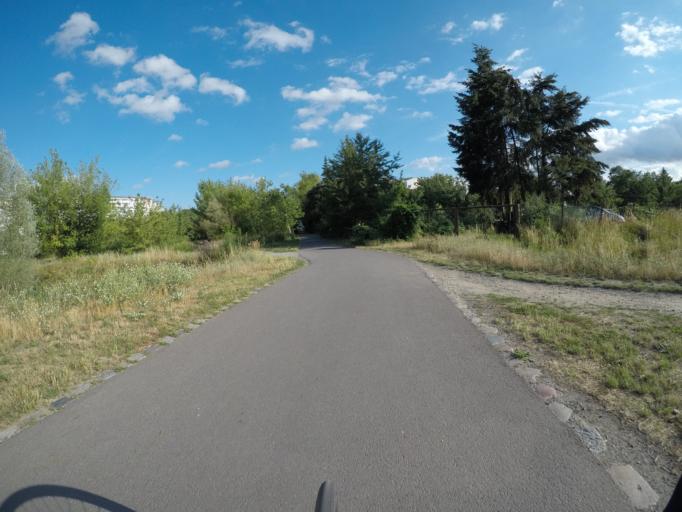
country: DE
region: Berlin
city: Stadtrandsiedlung Malchow
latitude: 52.5738
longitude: 13.4933
